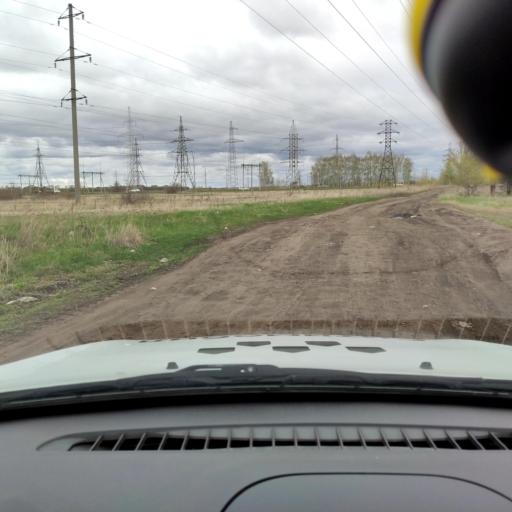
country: RU
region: Samara
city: Tol'yatti
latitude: 53.5858
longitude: 49.3286
